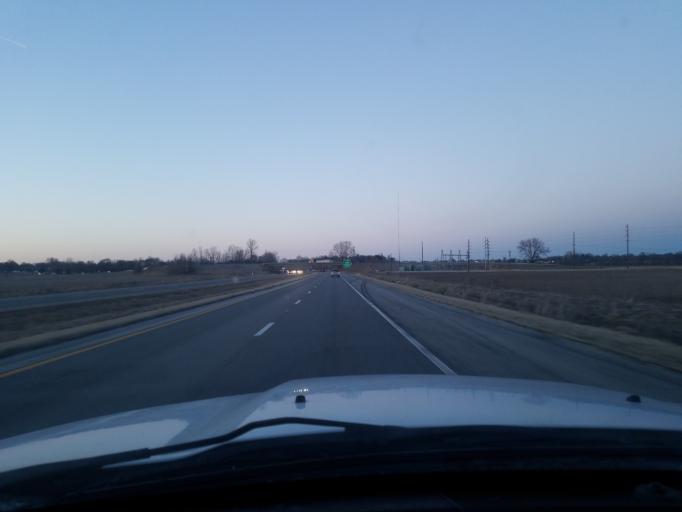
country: US
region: Kentucky
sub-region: Henderson County
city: Henderson
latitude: 37.8462
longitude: -87.5663
